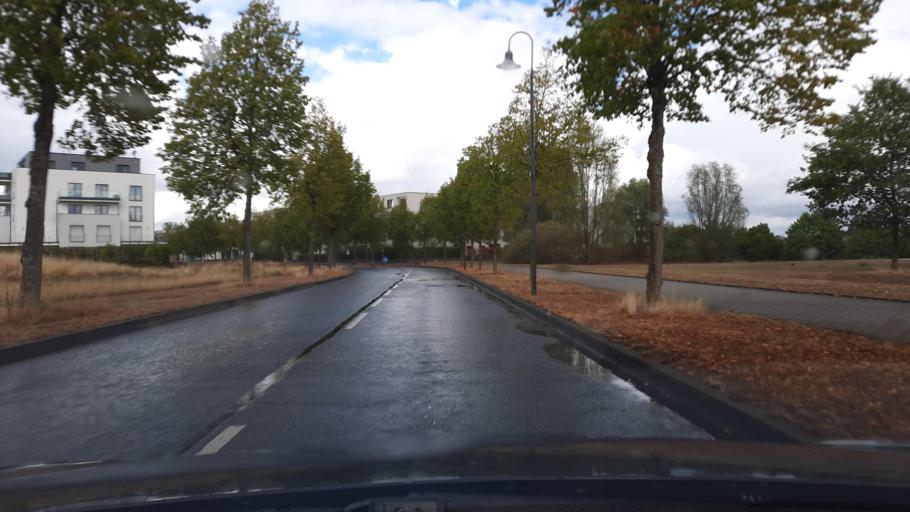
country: DE
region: Rheinland-Pfalz
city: Irsch
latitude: 49.7521
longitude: 6.6765
